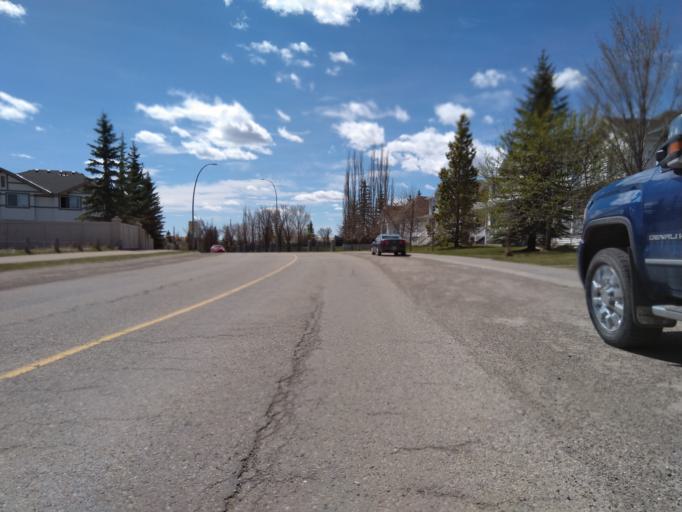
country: CA
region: Alberta
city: Calgary
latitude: 51.1266
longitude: -114.2437
